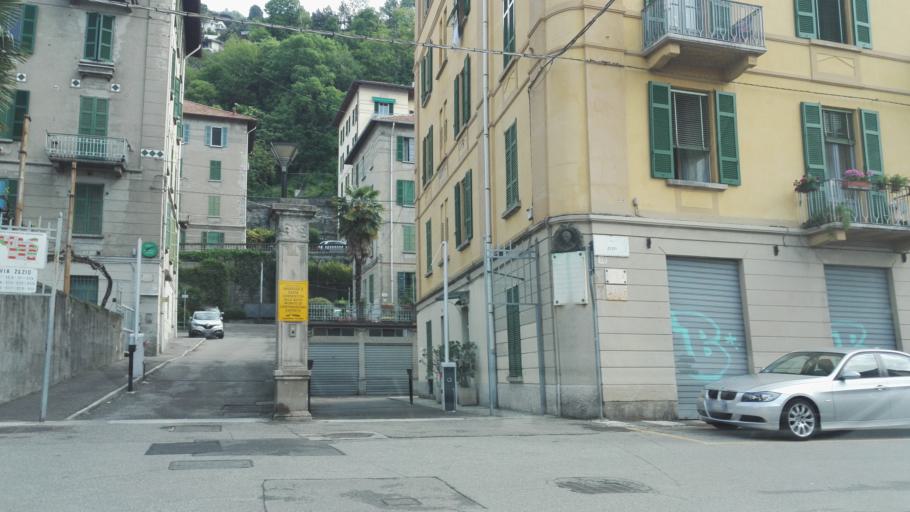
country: IT
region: Lombardy
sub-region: Provincia di Como
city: Brunate
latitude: 45.8075
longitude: 9.0962
